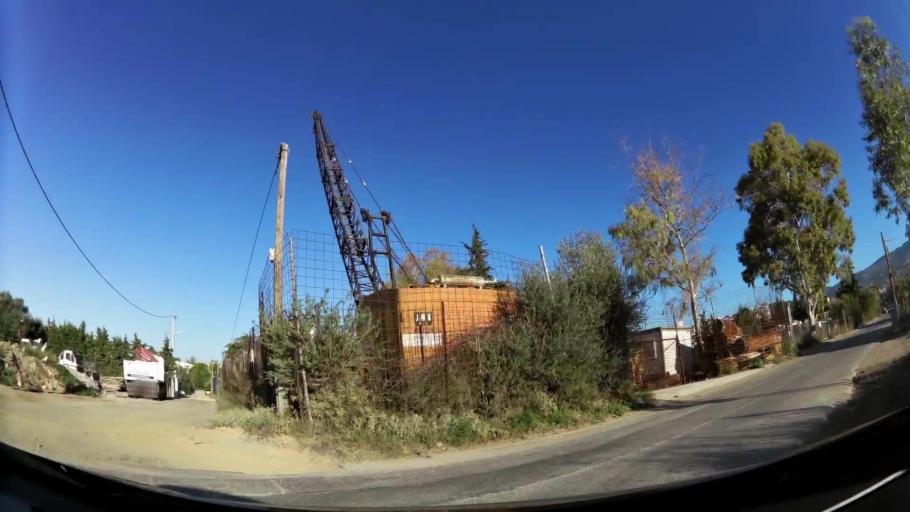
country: GR
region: Attica
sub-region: Nomarchia Anatolikis Attikis
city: Gerakas
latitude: 38.0358
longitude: 23.8467
